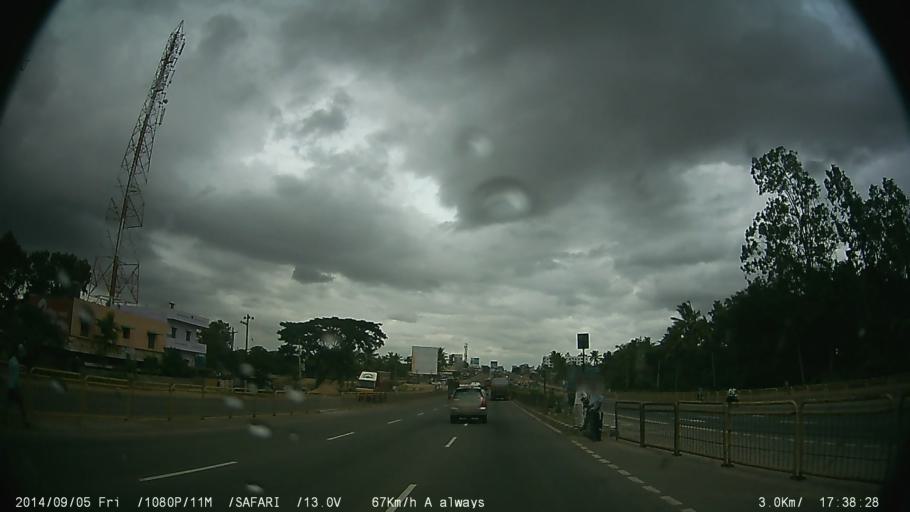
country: IN
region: Karnataka
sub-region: Bangalore Urban
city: Anekal
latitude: 12.7937
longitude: 77.7229
